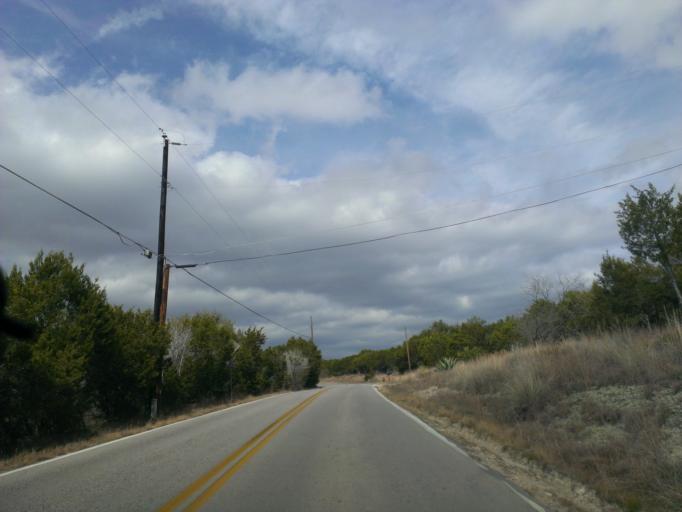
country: US
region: Texas
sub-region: Travis County
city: Briarcliff
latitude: 30.3718
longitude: -98.0855
